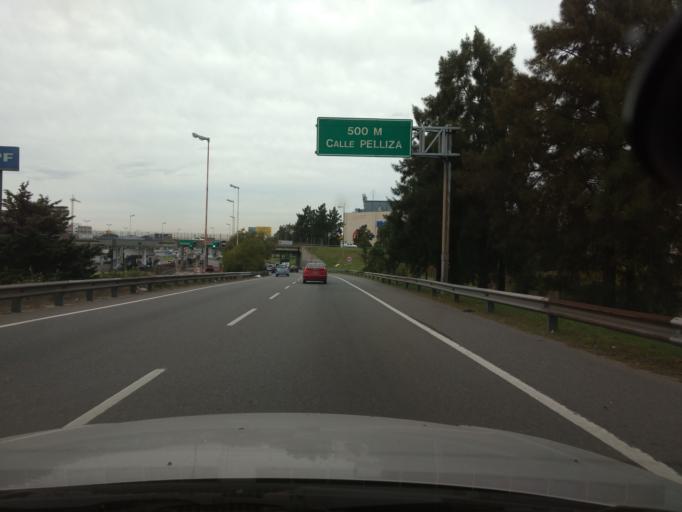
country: AR
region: Buenos Aires
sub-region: Partido de Vicente Lopez
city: Olivos
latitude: -34.5134
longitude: -58.5222
